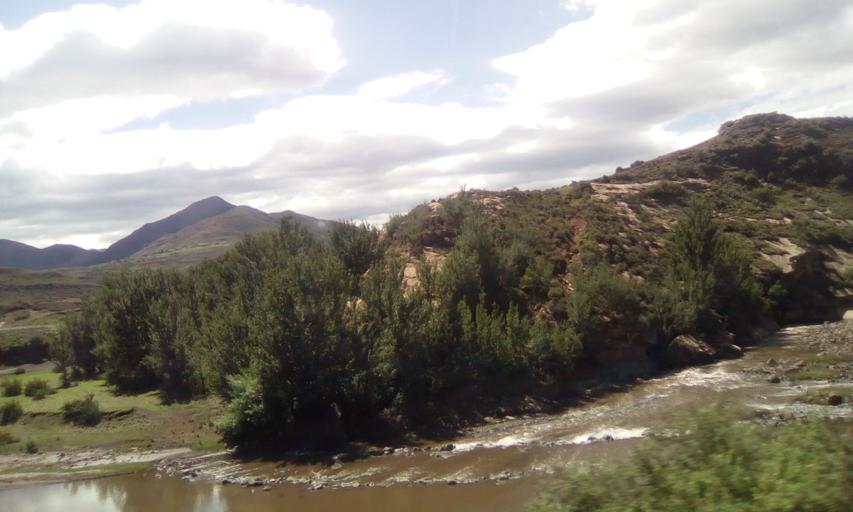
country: LS
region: Maseru
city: Nako
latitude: -29.6644
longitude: 27.8003
